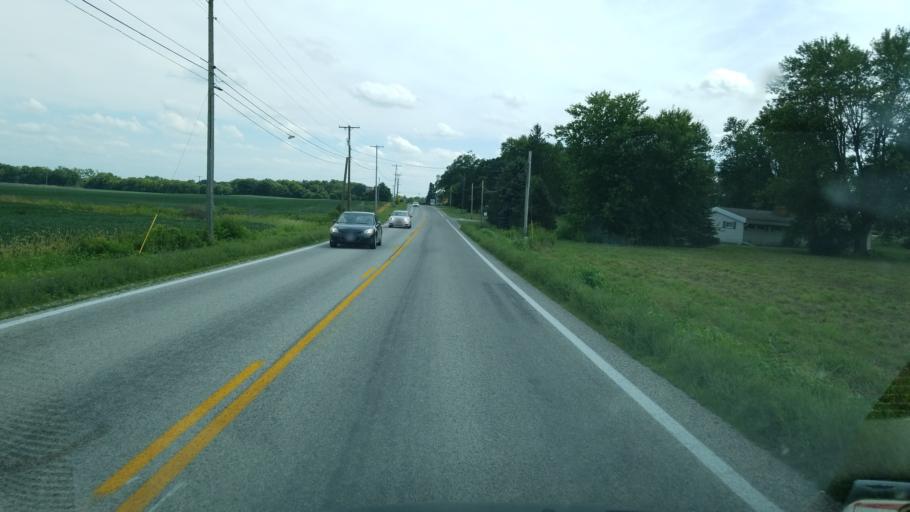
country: US
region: Ohio
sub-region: Marion County
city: Marion
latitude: 40.5234
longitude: -83.1013
